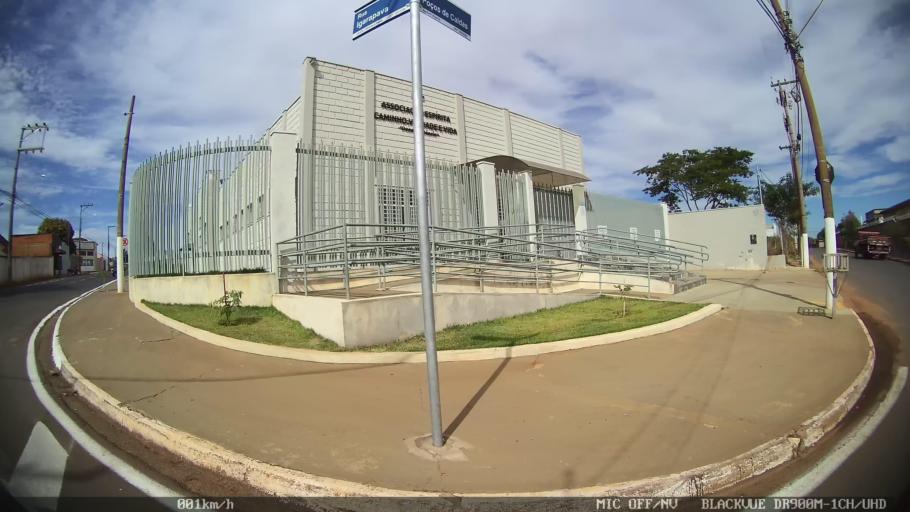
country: BR
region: Sao Paulo
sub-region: Catanduva
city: Catanduva
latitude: -21.1583
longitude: -48.9751
